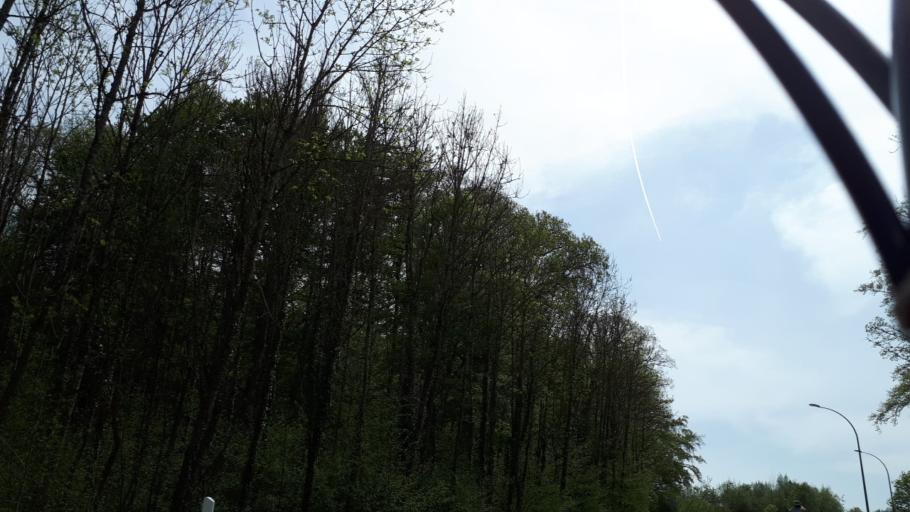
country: LU
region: Luxembourg
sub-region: Canton d'Esch-sur-Alzette
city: Leudelange
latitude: 49.5893
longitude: 6.0590
